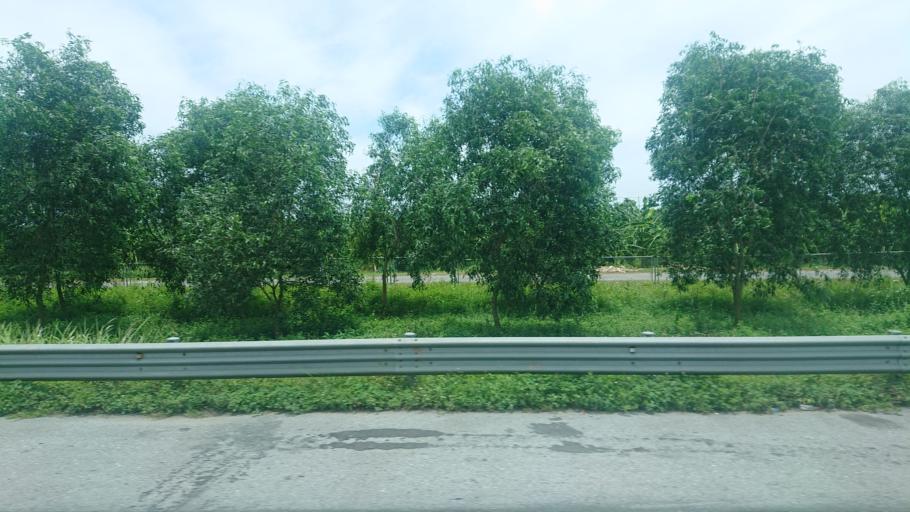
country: VN
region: Hai Phong
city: An Lao
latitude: 20.8167
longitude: 106.4890
